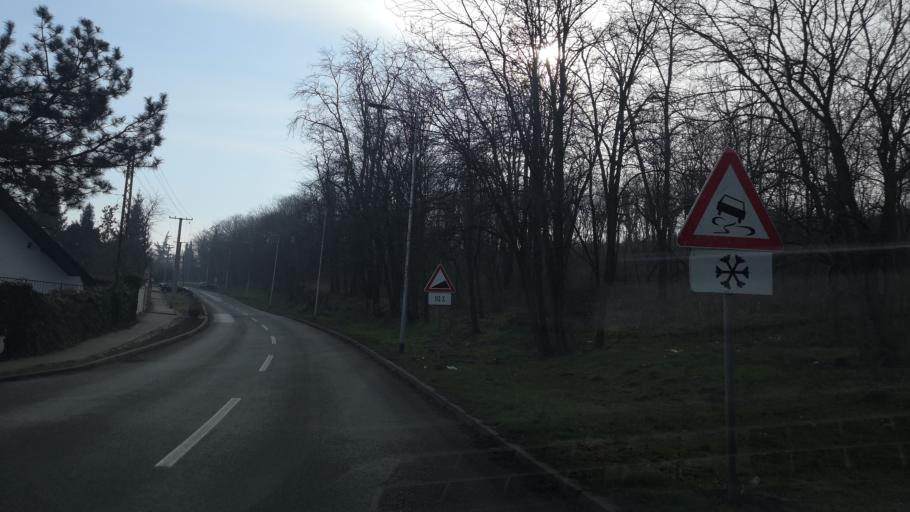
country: RS
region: Autonomna Pokrajina Vojvodina
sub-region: Juznobacki Okrug
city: Petrovaradin
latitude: 45.2488
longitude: 19.8734
